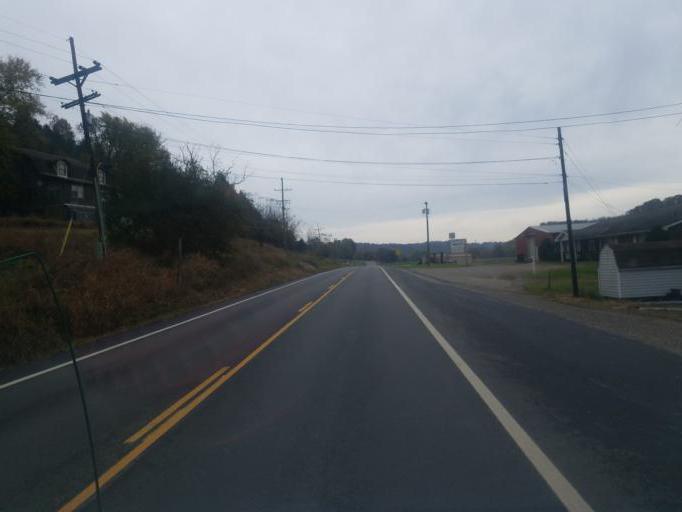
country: US
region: Ohio
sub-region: Washington County
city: Devola
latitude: 39.5253
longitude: -81.4991
